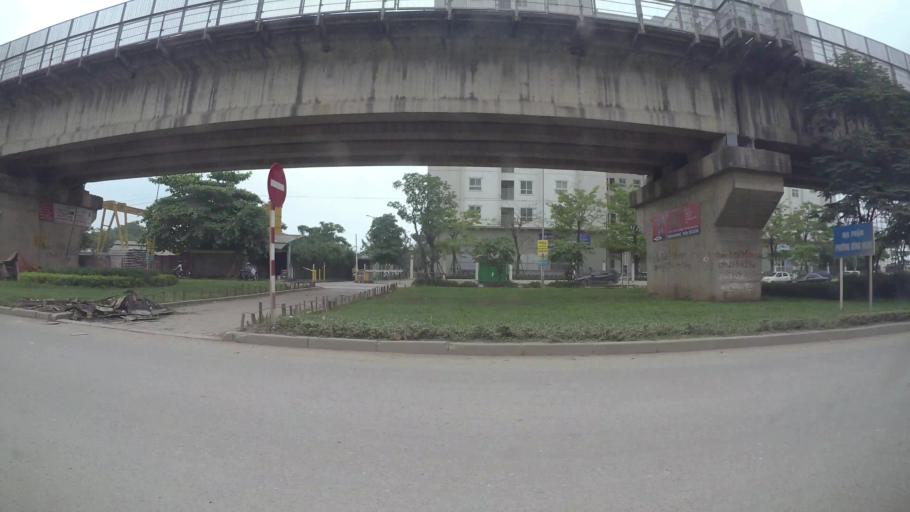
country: VN
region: Ha Noi
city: Tay Ho
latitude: 21.0834
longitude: 105.7854
